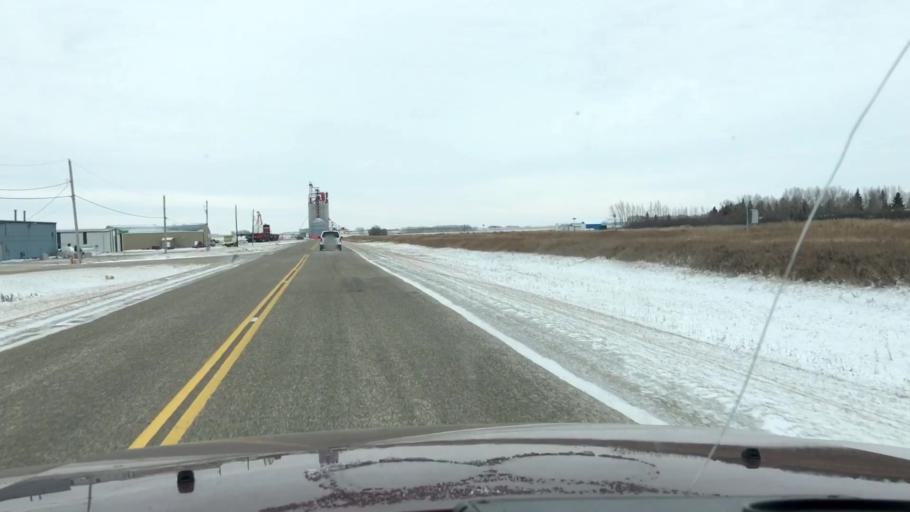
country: CA
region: Saskatchewan
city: Watrous
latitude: 51.2536
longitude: -105.9820
